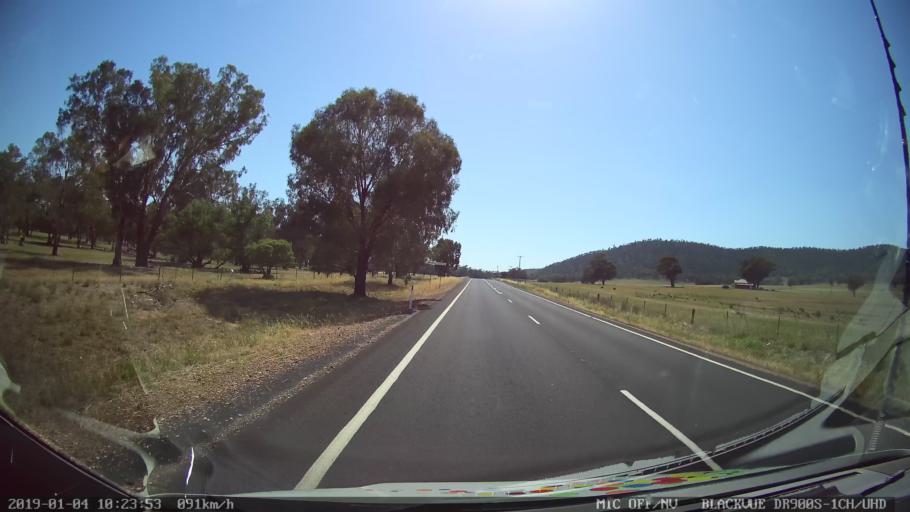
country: AU
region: New South Wales
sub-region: Cabonne
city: Canowindra
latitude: -33.3700
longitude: 148.5461
